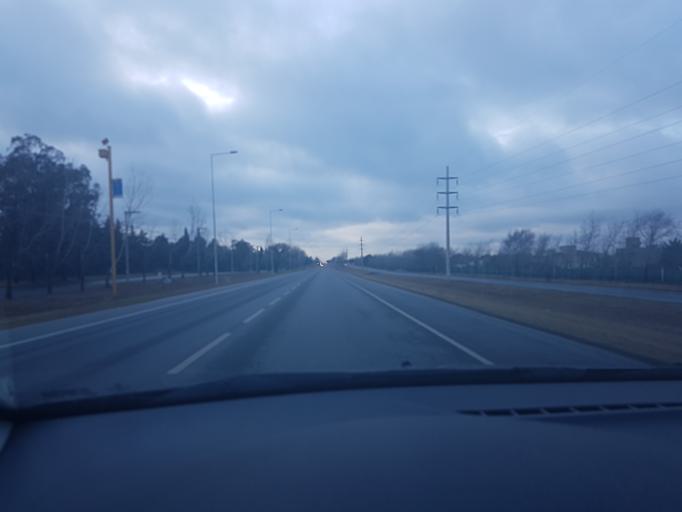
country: AR
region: Cordoba
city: Villa Allende
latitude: -31.3020
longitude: -64.2557
